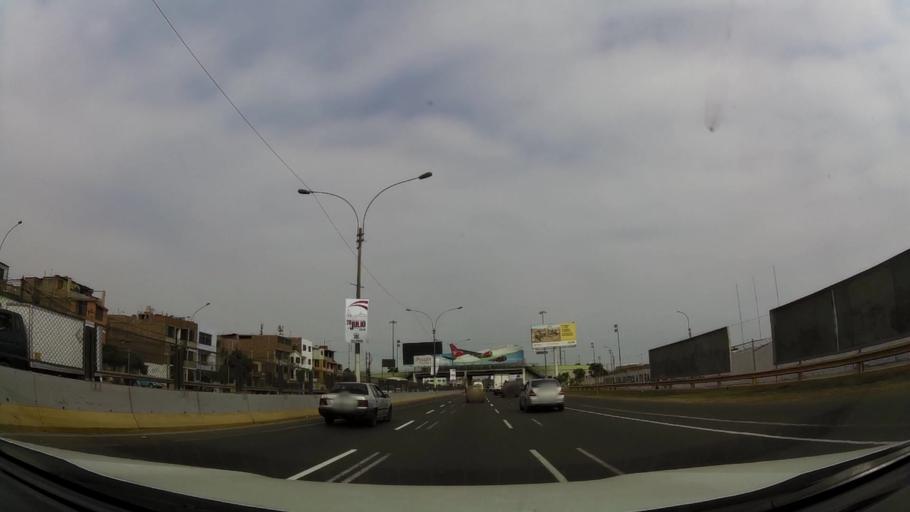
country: PE
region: Callao
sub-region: Callao
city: Callao
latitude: -12.0346
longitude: -77.0999
